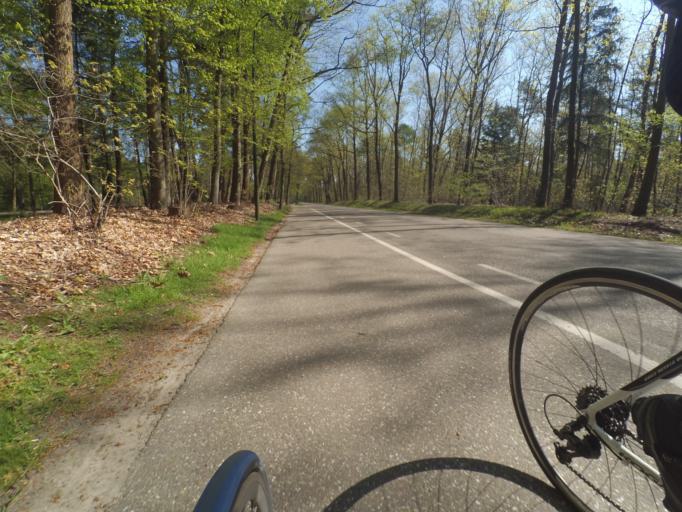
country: NL
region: Gelderland
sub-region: Gemeente Apeldoorn
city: Beekbergen
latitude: 52.1738
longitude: 5.9144
